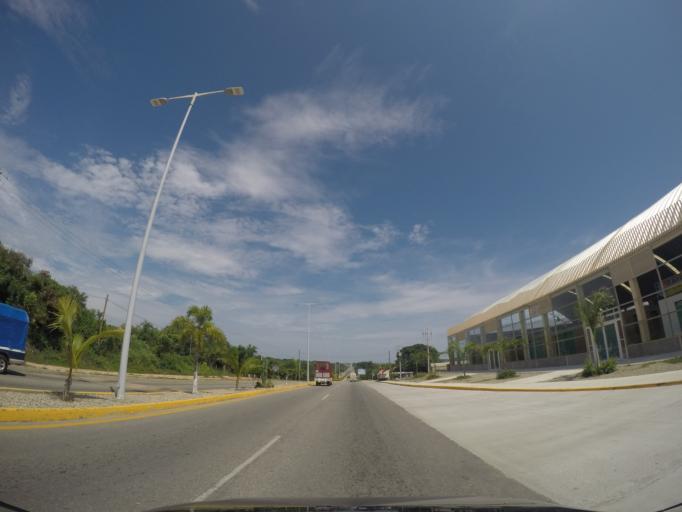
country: MX
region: Oaxaca
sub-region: Santa Maria Colotepec
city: Brisas de Zicatela
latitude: 15.8480
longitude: -97.0486
